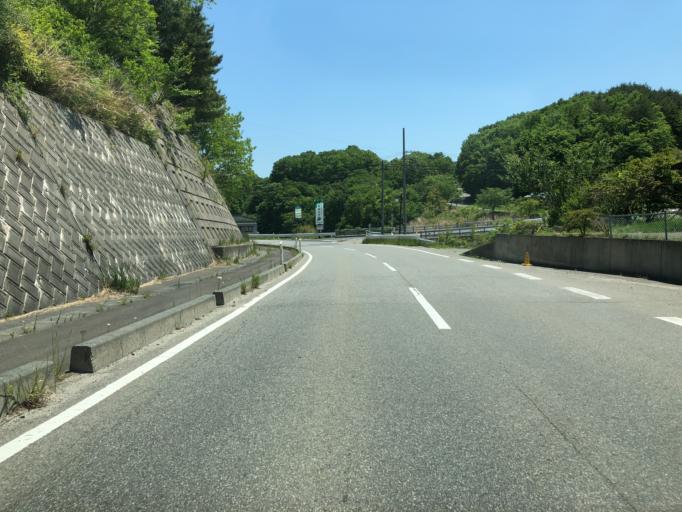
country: JP
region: Fukushima
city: Funehikimachi-funehiki
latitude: 37.5018
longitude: 140.7597
